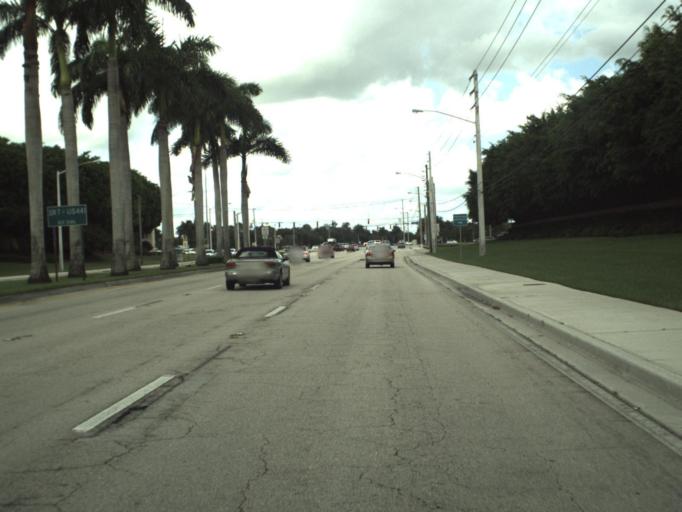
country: US
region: Florida
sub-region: Palm Beach County
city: Wellington
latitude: 26.6509
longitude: -80.2006
